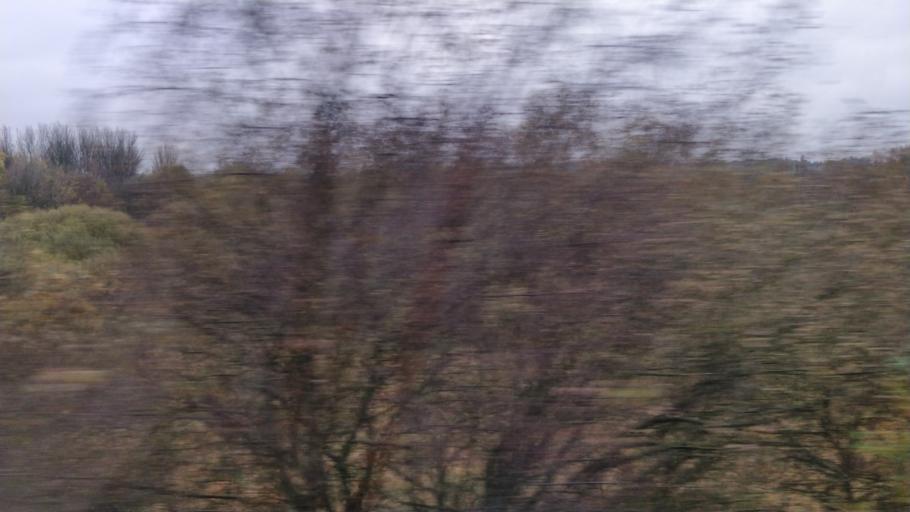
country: GB
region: England
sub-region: Borough of Wigan
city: Shevington
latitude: 53.5574
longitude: -2.6783
